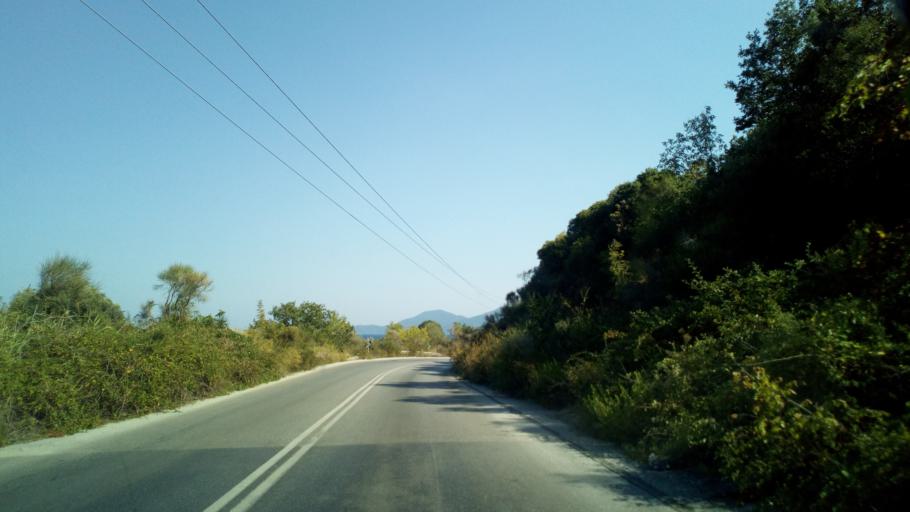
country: GR
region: Central Macedonia
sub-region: Nomos Thessalonikis
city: Stavros
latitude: 40.6125
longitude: 23.7780
